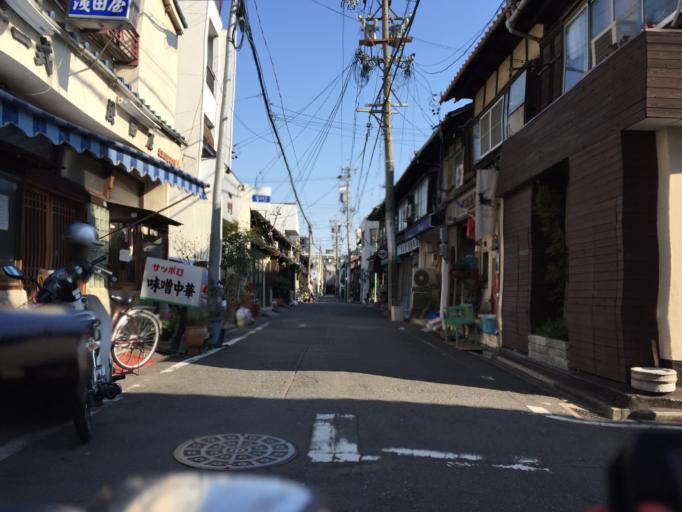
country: JP
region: Aichi
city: Nagoya-shi
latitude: 35.1748
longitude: 136.8914
